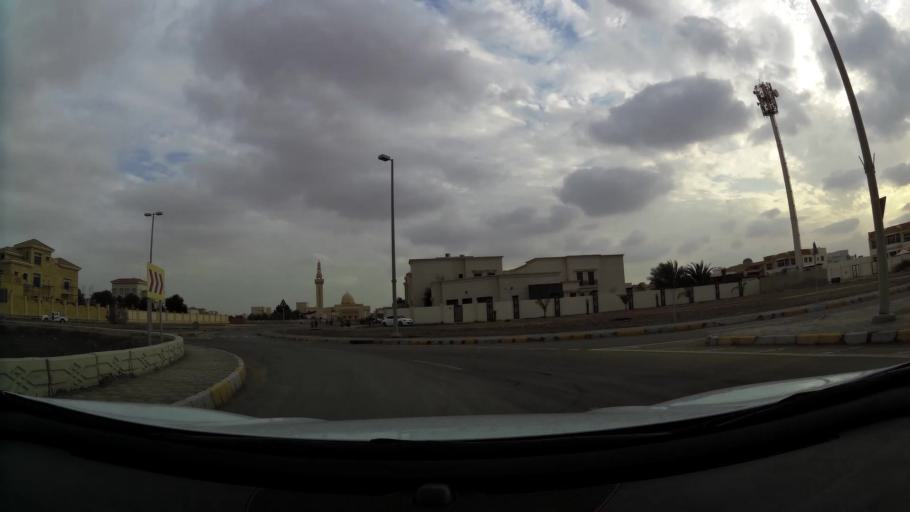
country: AE
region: Abu Dhabi
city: Abu Dhabi
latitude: 24.3558
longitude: 54.5453
